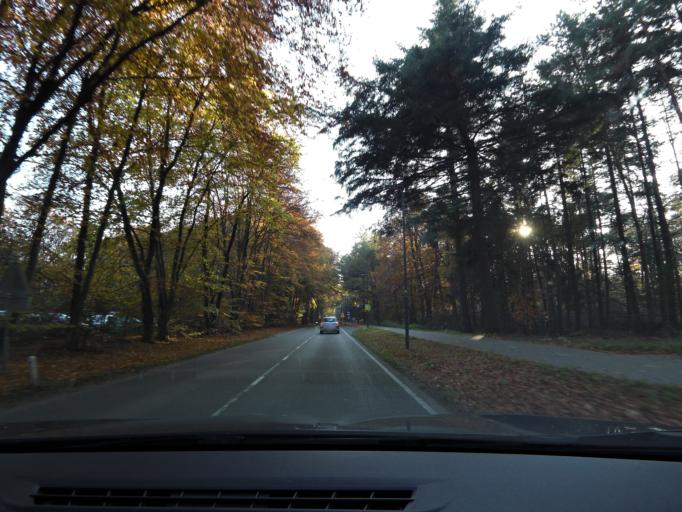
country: NL
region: North Brabant
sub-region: Gemeente Breda
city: Breda
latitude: 51.5502
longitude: 4.7788
